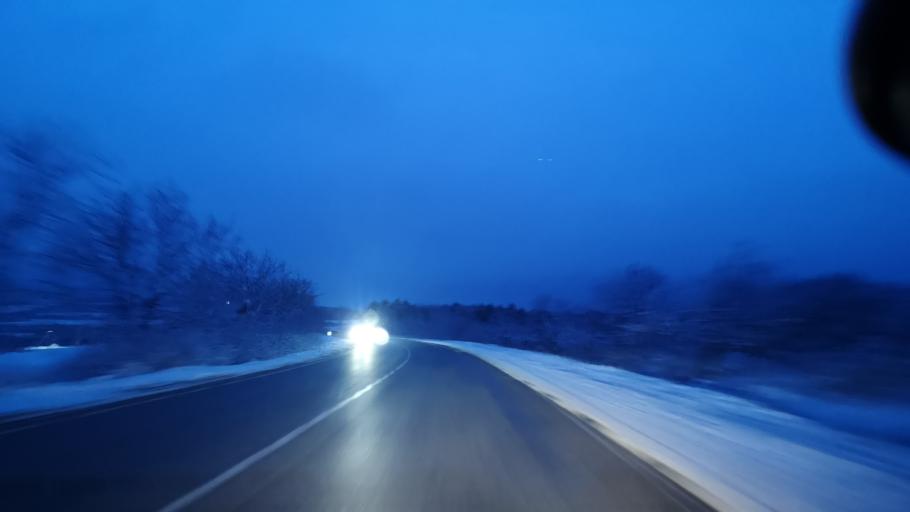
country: MD
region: Orhei
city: Orhei
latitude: 47.5497
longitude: 28.7930
